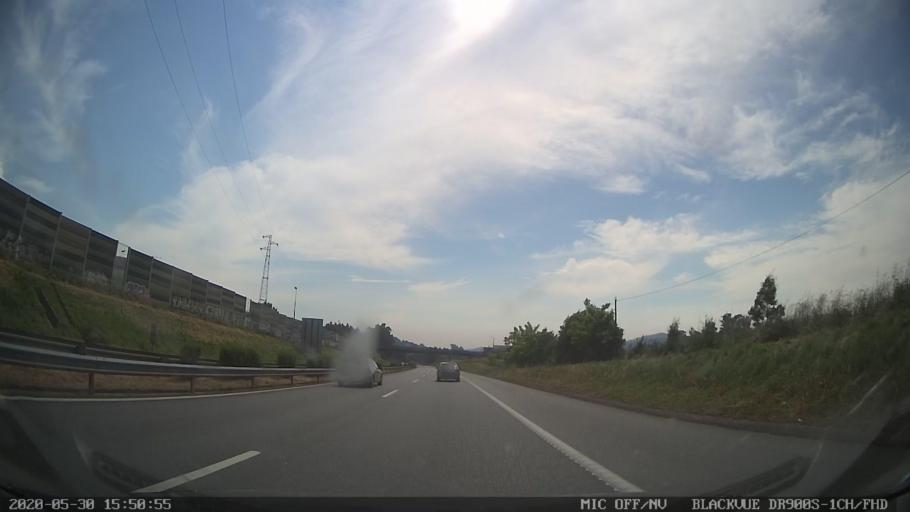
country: PT
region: Porto
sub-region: Penafiel
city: Penafiel
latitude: 41.2064
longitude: -8.2977
